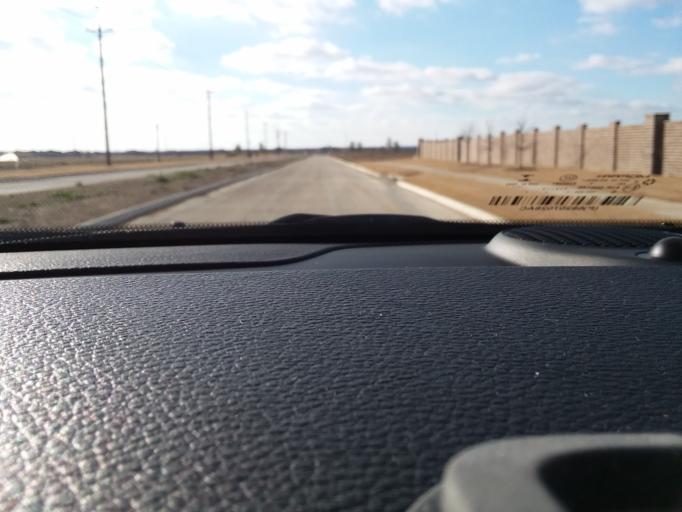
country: US
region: Texas
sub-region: Collin County
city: Prosper
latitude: 33.2677
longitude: -96.8896
